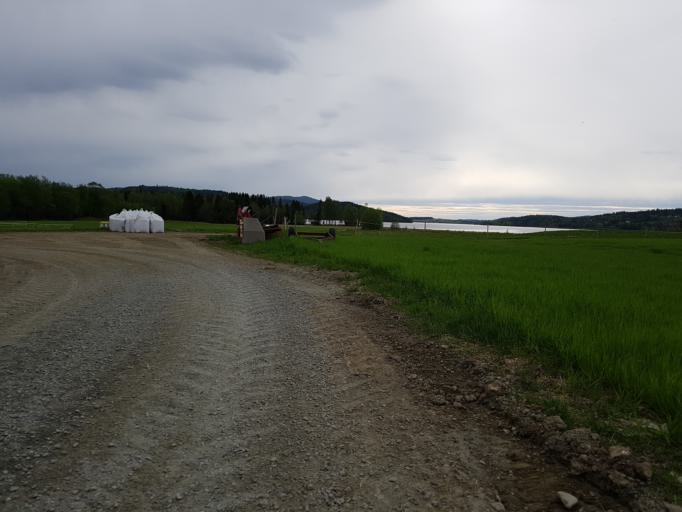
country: NO
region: Nord-Trondelag
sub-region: Levanger
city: Skogn
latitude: 63.6304
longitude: 11.2596
